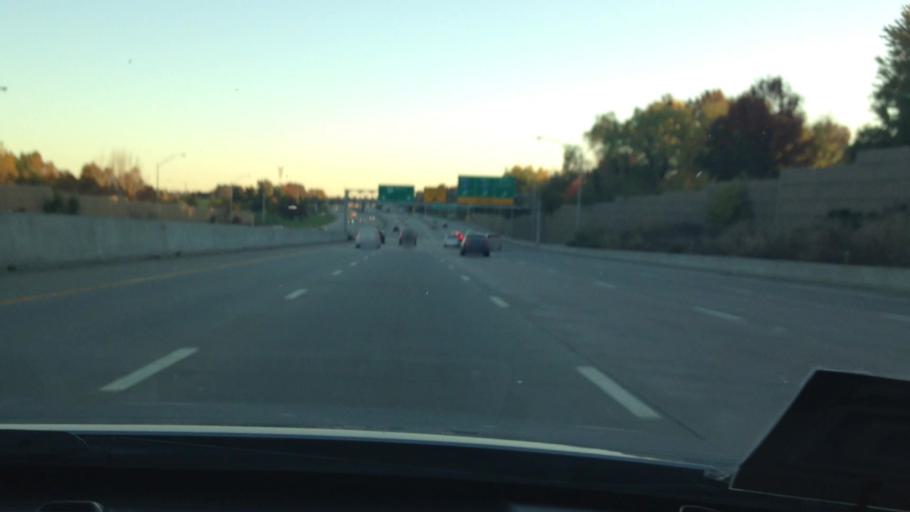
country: US
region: Kansas
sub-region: Johnson County
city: Lenexa
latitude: 38.9485
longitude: -94.7056
